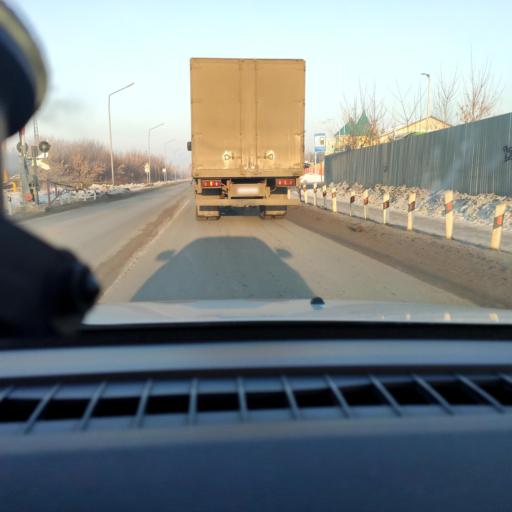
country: RU
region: Samara
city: Chapayevsk
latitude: 52.9694
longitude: 49.6971
